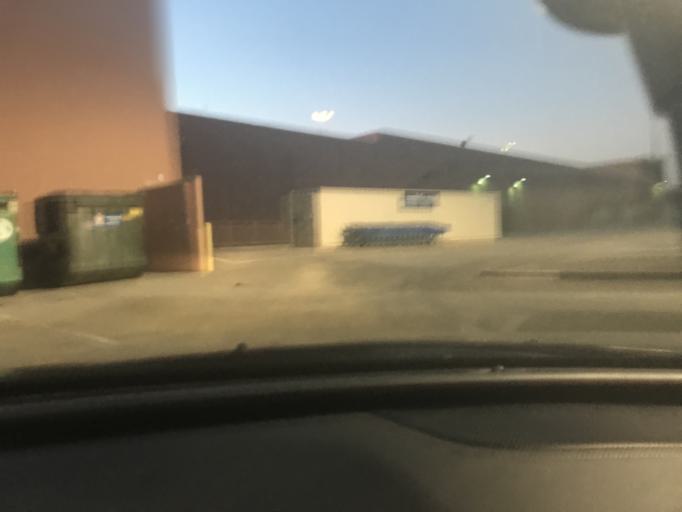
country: US
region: Texas
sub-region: Tarrant County
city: Arlington
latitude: 32.7574
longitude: -97.0996
